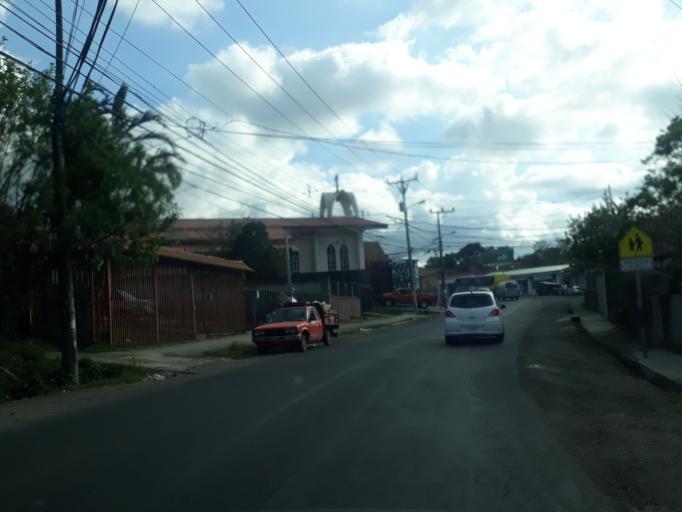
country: CR
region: San Jose
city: Purral
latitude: 9.9754
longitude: -84.0320
